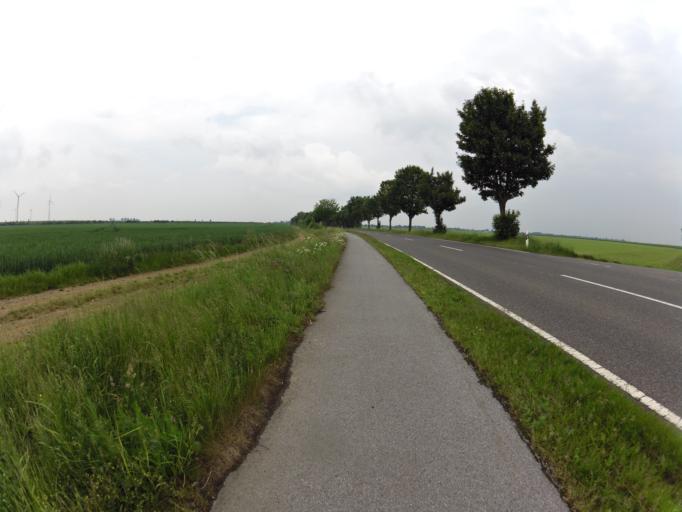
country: DE
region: North Rhine-Westphalia
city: Baesweiler
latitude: 50.9314
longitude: 6.1635
